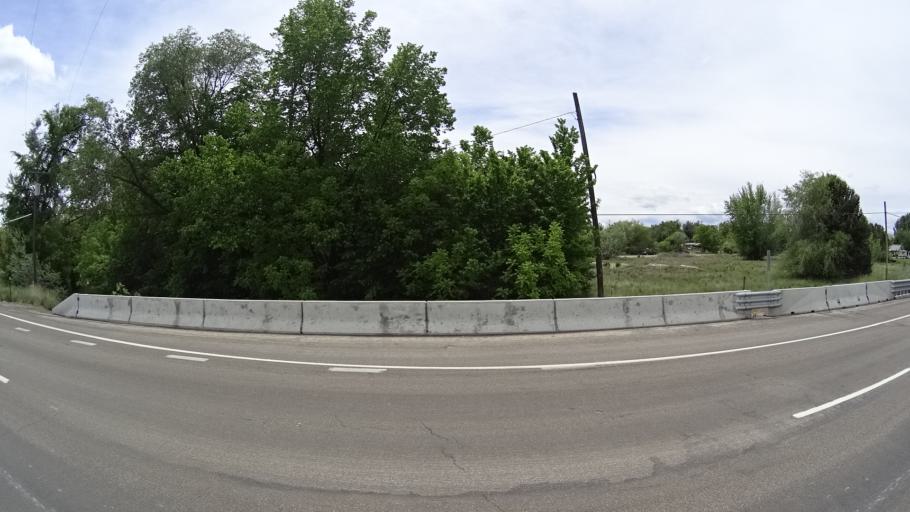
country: US
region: Idaho
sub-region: Ada County
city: Eagle
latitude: 43.6951
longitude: -116.4052
